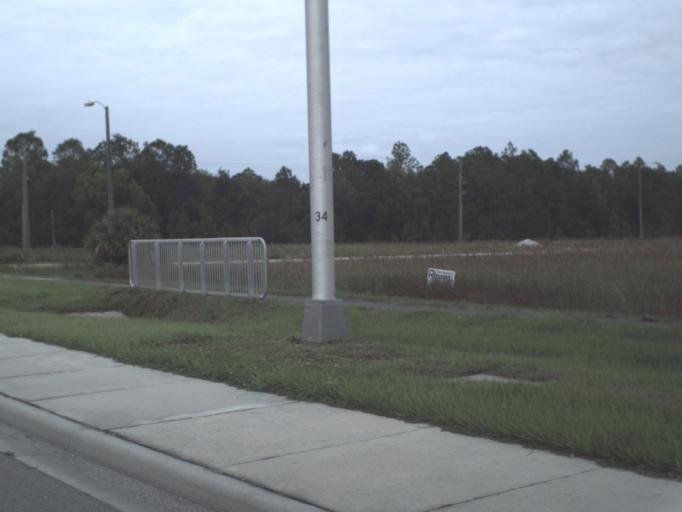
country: US
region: Florida
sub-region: Collier County
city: Golden Gate
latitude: 26.1549
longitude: -81.6895
